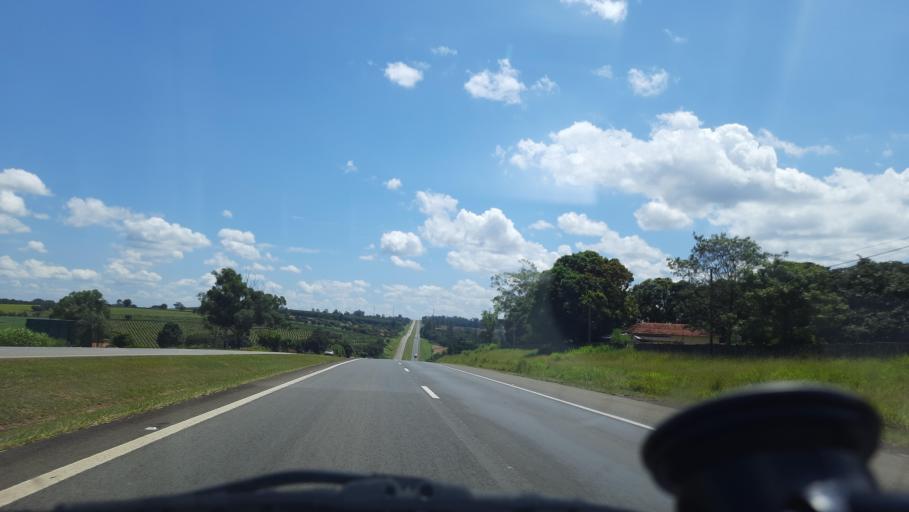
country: BR
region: Sao Paulo
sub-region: Moji-Guacu
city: Mogi-Gaucu
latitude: -22.2545
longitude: -46.9773
